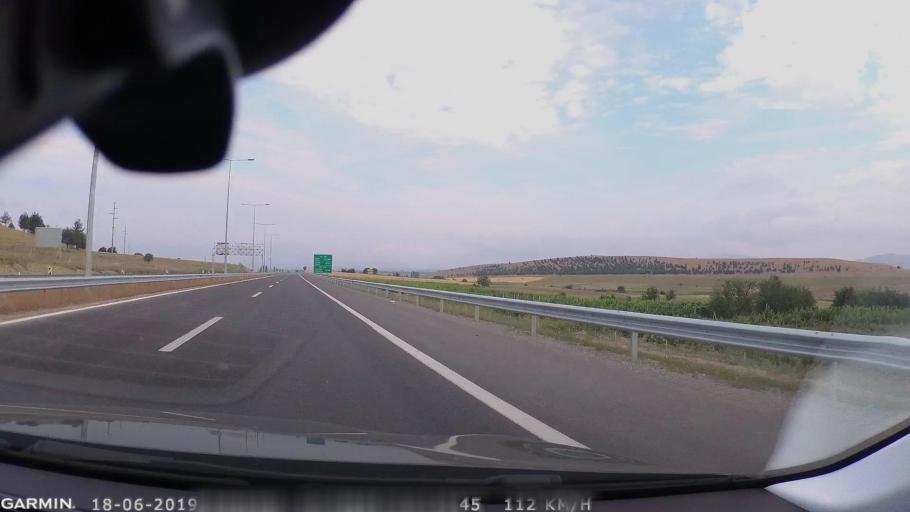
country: MK
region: Stip
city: Shtip
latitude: 41.7841
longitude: 22.1217
